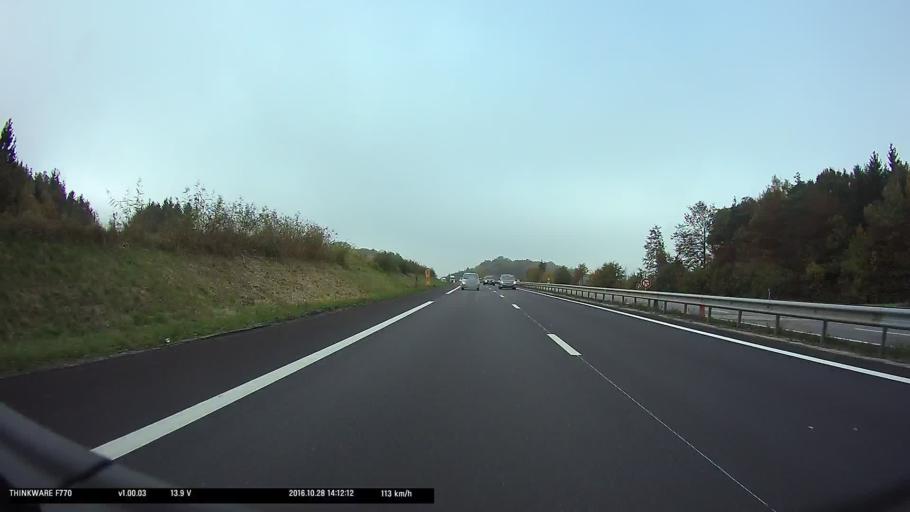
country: FR
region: Lorraine
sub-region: Departement de Meurthe-et-Moselle
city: Damelevieres
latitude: 48.5910
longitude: 6.4221
